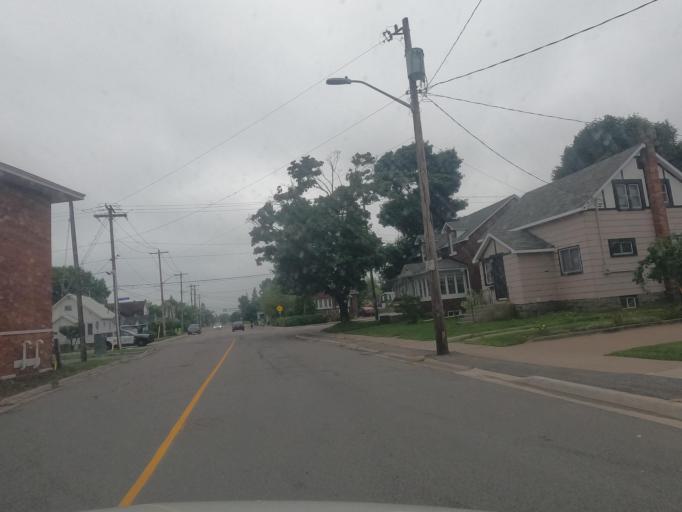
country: CA
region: Ontario
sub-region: Algoma
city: Sault Ste. Marie
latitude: 46.5250
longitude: -84.3462
